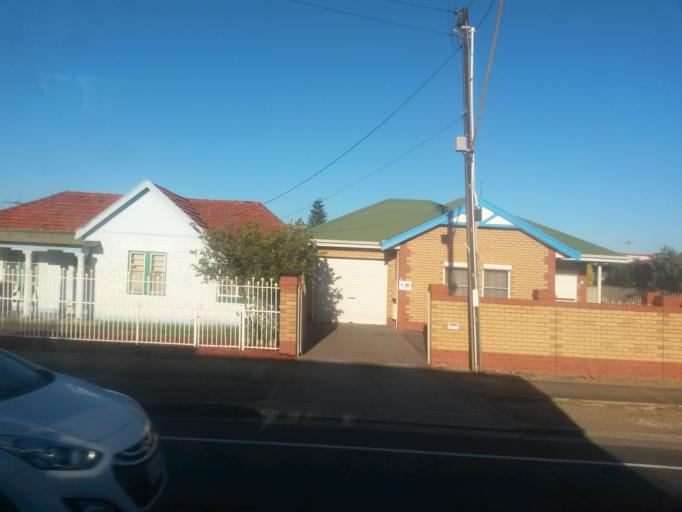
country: AU
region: South Australia
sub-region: Port Adelaide Enfield
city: Alberton
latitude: -34.8551
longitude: 138.5291
